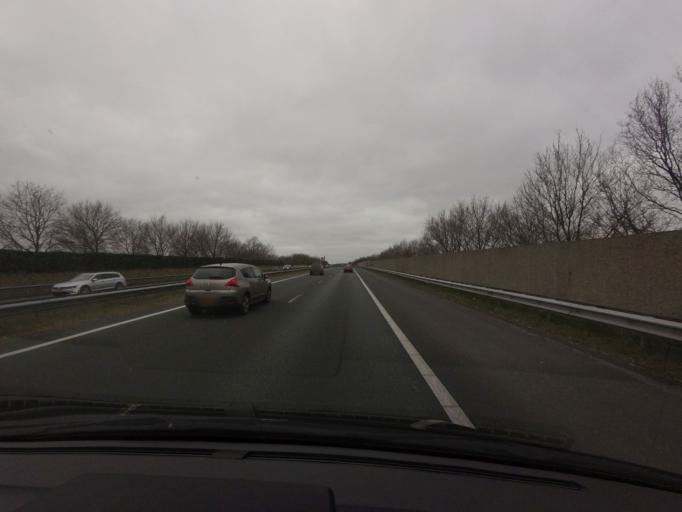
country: NL
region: Groningen
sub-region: Gemeente Hoogezand-Sappemeer
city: Sappemeer
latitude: 53.1685
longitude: 6.7913
